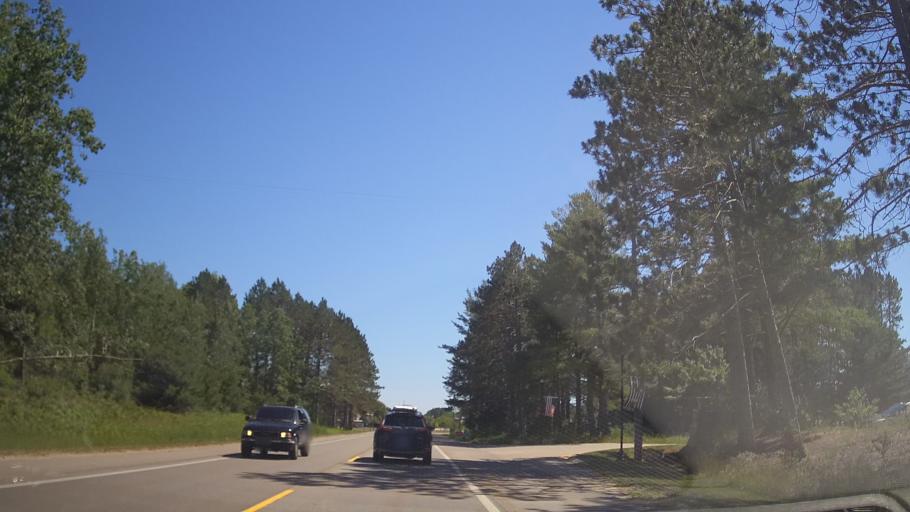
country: US
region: Michigan
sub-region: Cheboygan County
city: Indian River
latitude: 45.5574
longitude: -84.7843
